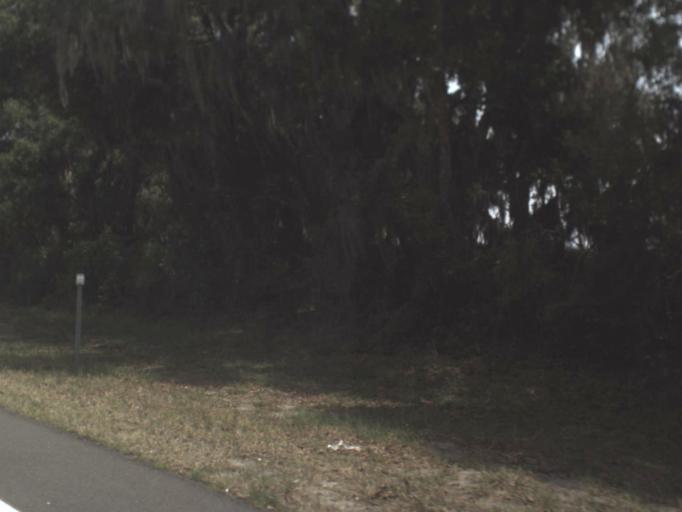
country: US
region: Florida
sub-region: Duval County
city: Atlantic Beach
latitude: 30.4636
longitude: -81.4329
